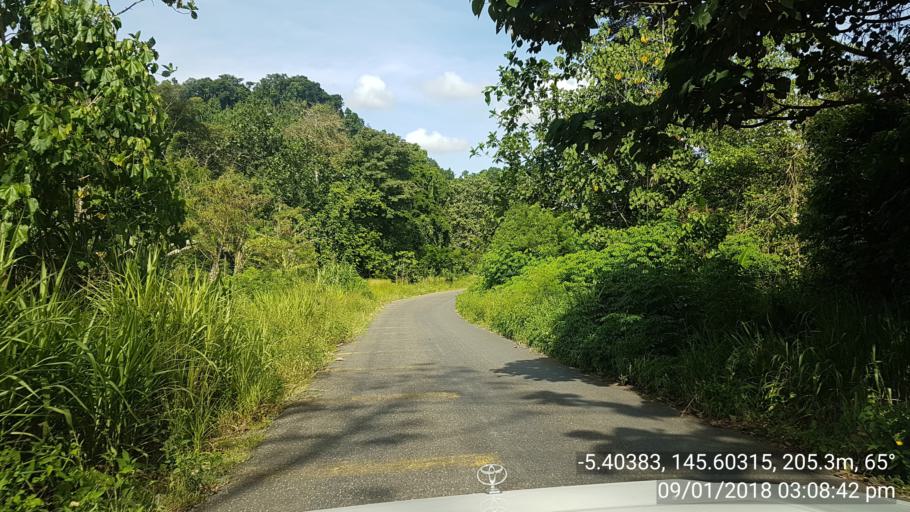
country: PG
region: Madang
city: Madang
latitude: -5.4039
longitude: 145.6031
